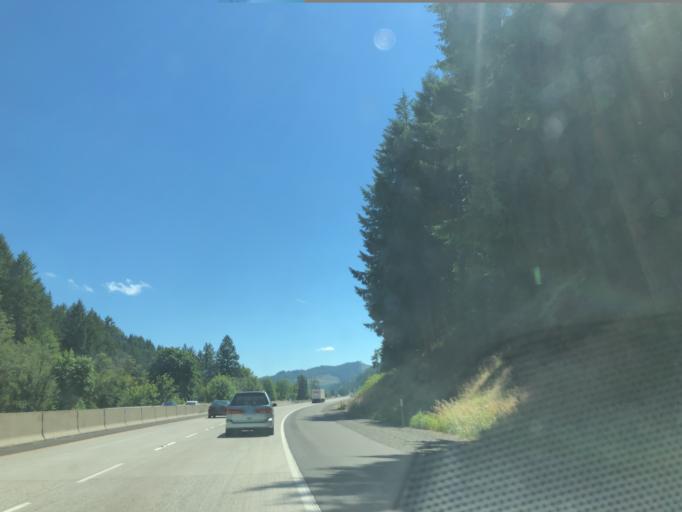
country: US
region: Oregon
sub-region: Douglas County
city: Yoncalla
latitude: 43.6616
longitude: -123.2031
